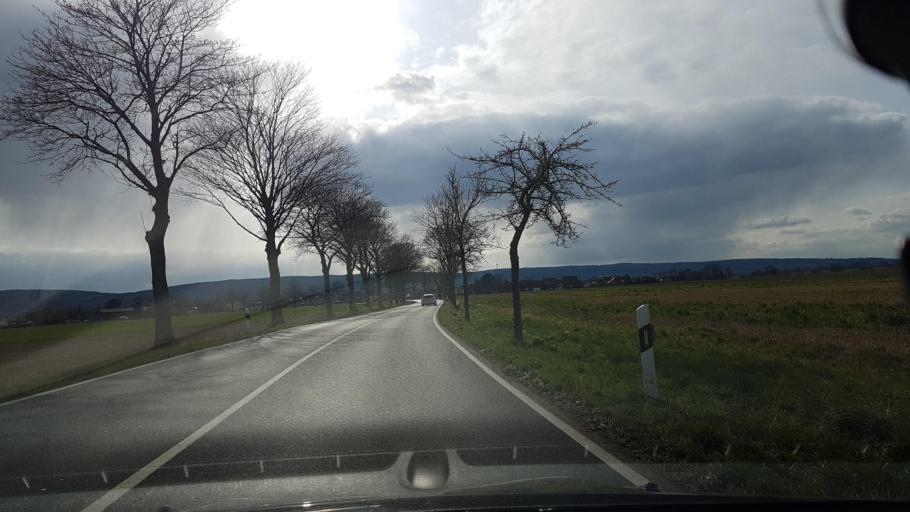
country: DE
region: Lower Saxony
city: Egestorf
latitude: 52.3101
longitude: 9.5446
